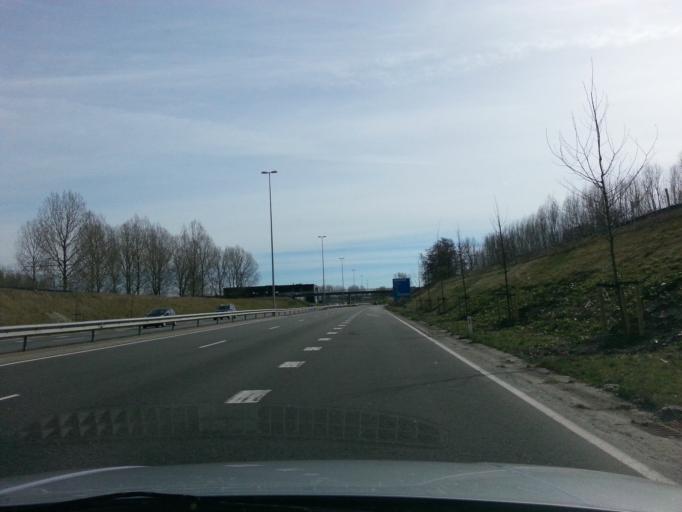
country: NL
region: Groningen
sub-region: Gemeente Groningen
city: Oosterpark
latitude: 53.2405
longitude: 6.5869
